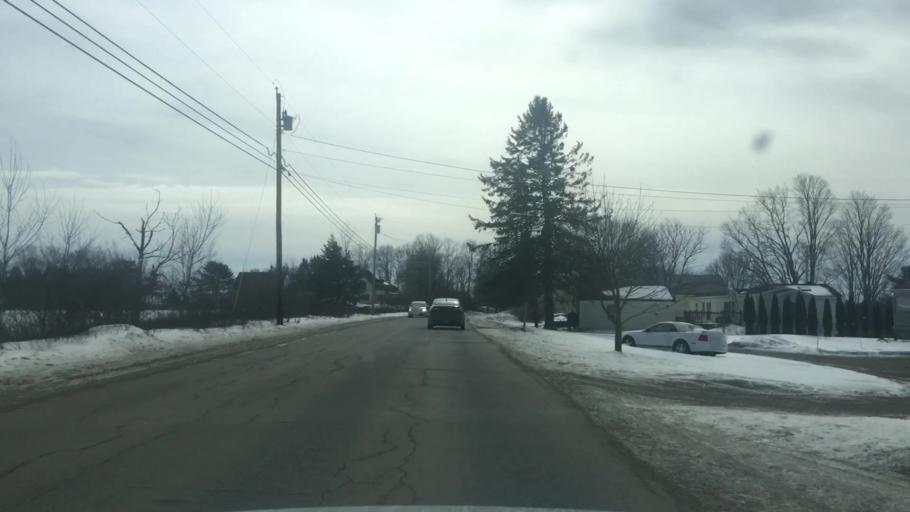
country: US
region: Maine
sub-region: Hancock County
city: Orland
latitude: 44.5790
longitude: -68.7254
